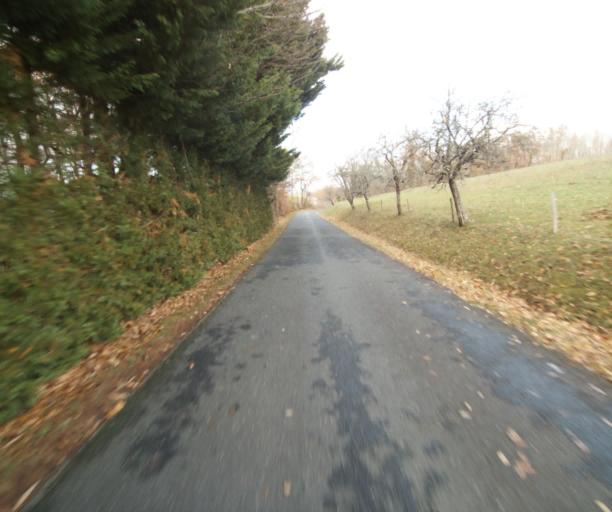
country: FR
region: Limousin
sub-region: Departement de la Correze
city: Laguenne
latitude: 45.2278
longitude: 1.7912
